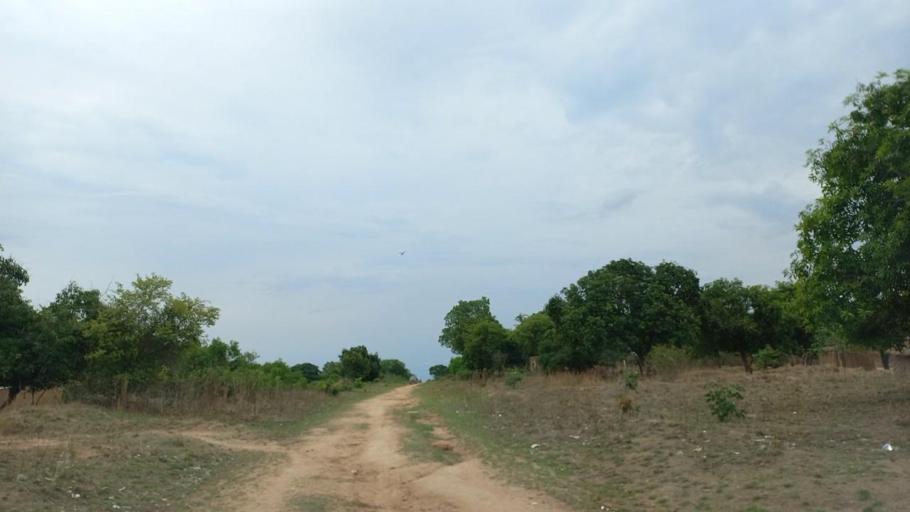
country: ZM
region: North-Western
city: Kalengwa
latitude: -13.6432
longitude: 24.9805
